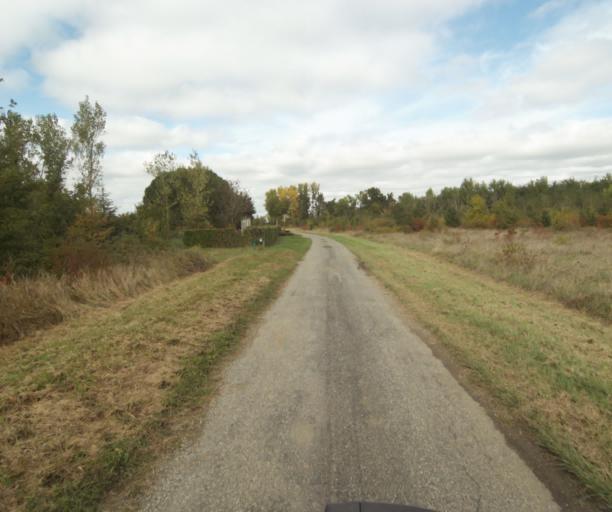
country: FR
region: Midi-Pyrenees
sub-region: Departement du Tarn-et-Garonne
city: Finhan
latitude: 43.9254
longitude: 1.2083
